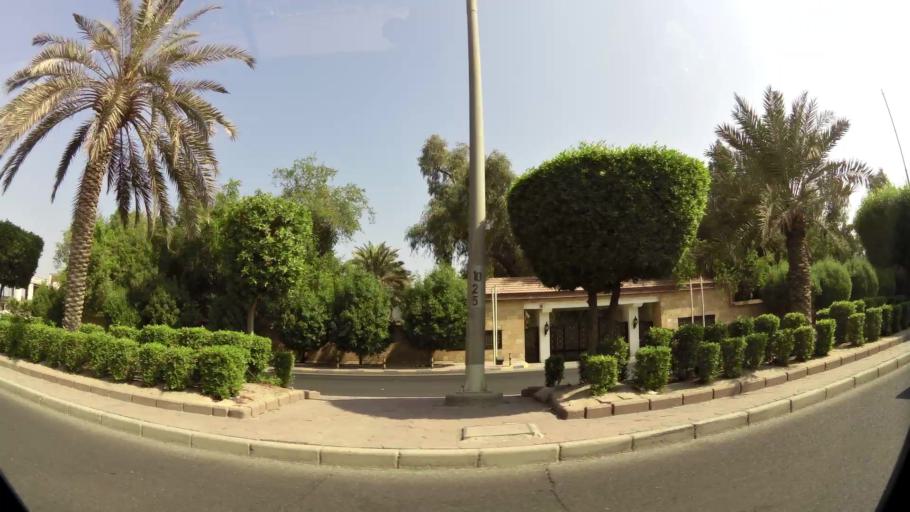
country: KW
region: Al Ahmadi
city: Al Mahbulah
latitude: 29.1469
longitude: 48.1278
